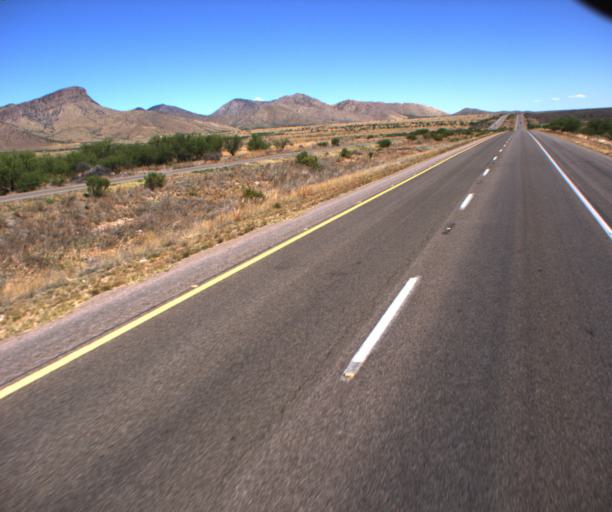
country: US
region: Arizona
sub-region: Cochise County
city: Huachuca City
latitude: 31.7835
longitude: -110.3499
